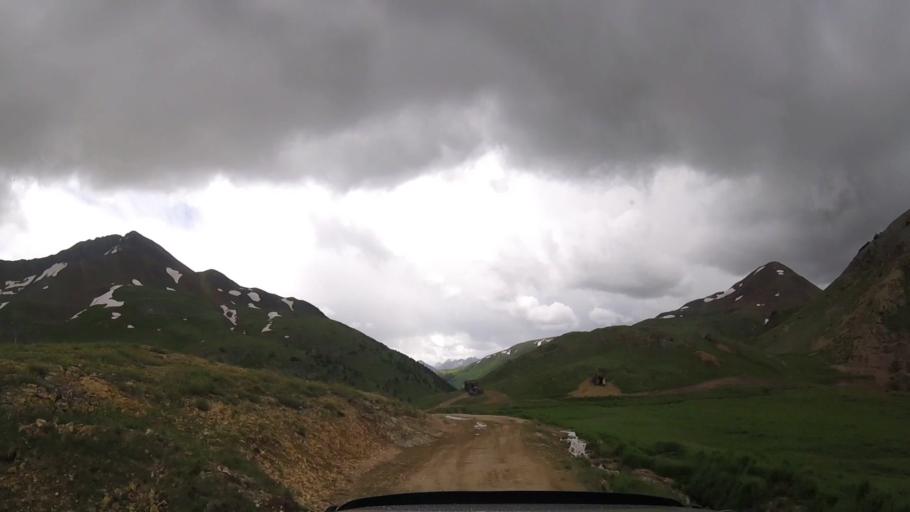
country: US
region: Colorado
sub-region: Ouray County
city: Ouray
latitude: 37.9530
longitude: -107.5746
